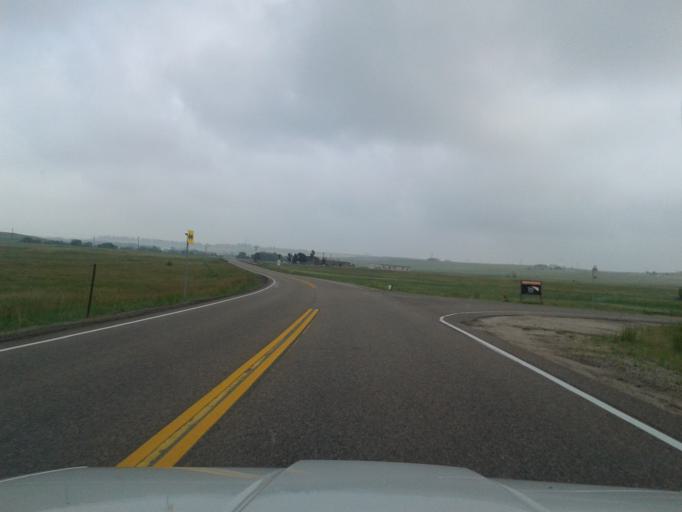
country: US
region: Colorado
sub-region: Elbert County
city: Elizabeth
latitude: 39.2238
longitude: -104.7006
